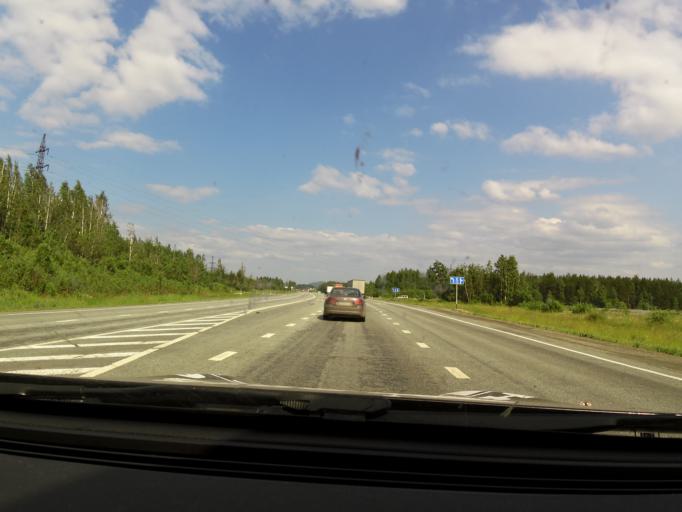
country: RU
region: Sverdlovsk
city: Revda
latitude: 56.8262
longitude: 59.8762
